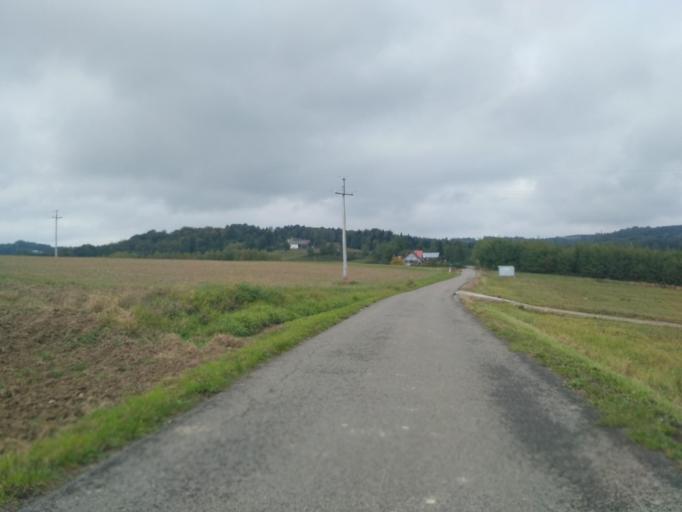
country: PL
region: Subcarpathian Voivodeship
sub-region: Powiat debicki
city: Brzostek
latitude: 49.9407
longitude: 21.4517
